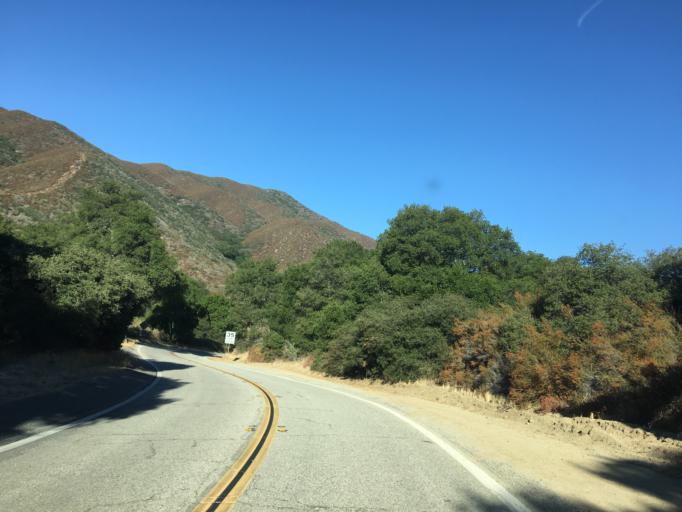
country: US
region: California
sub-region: Los Angeles County
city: Green Valley
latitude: 34.6100
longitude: -118.3923
